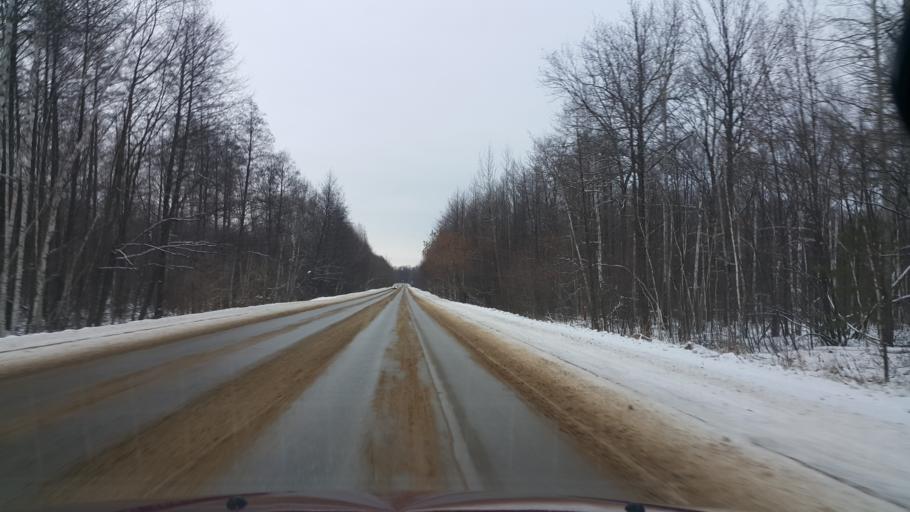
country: RU
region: Tambov
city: Kotovsk
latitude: 52.6239
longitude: 41.5142
